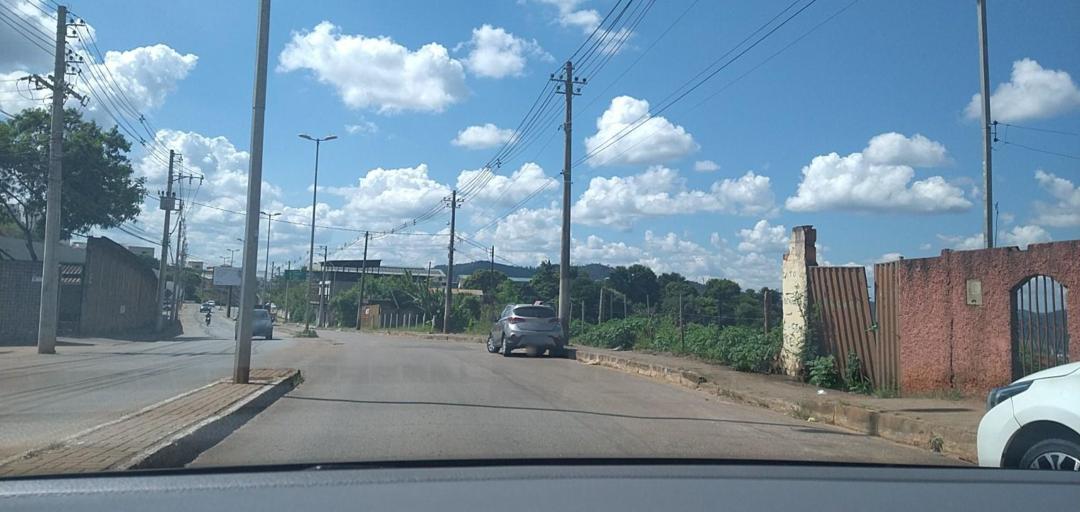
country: BR
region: Minas Gerais
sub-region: Joao Monlevade
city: Joao Monlevade
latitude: -19.8297
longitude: -43.1879
